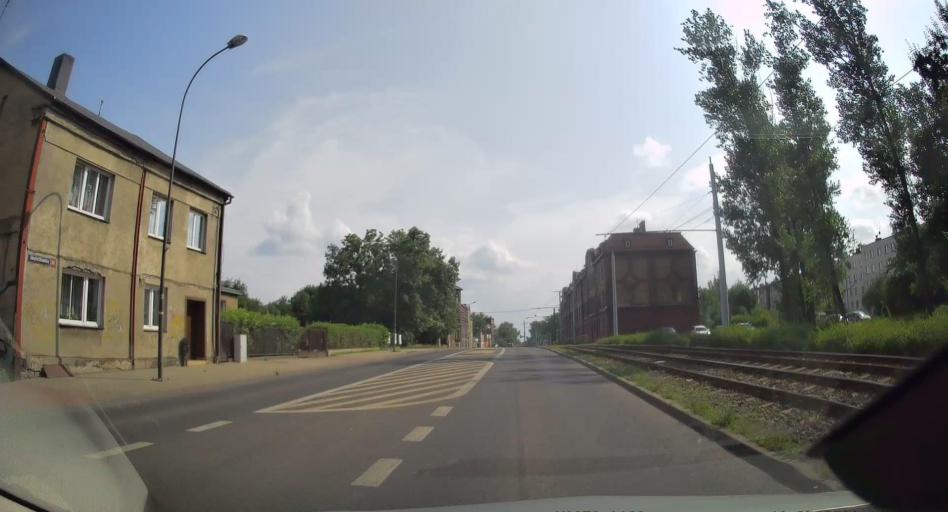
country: PL
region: Silesian Voivodeship
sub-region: Bytom
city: Bytom
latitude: 50.3227
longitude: 18.9269
